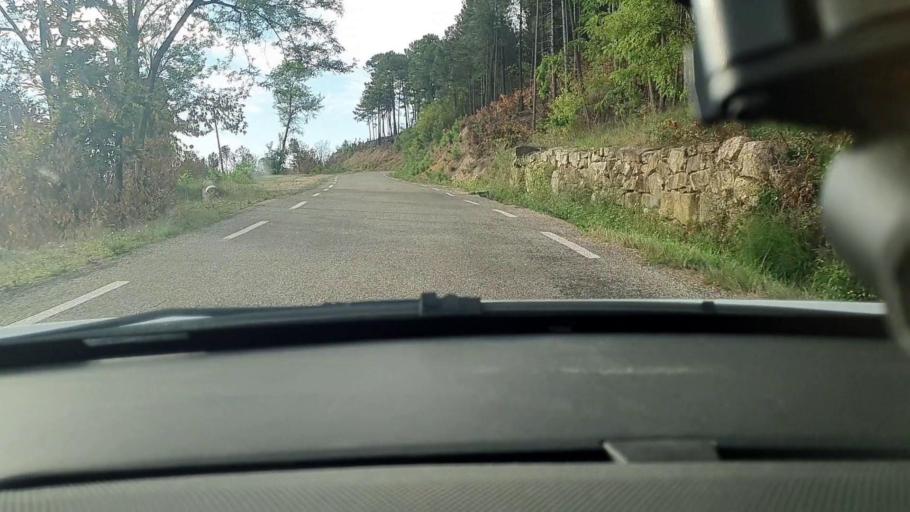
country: FR
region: Languedoc-Roussillon
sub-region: Departement du Gard
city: Besseges
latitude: 44.3105
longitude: 4.0877
